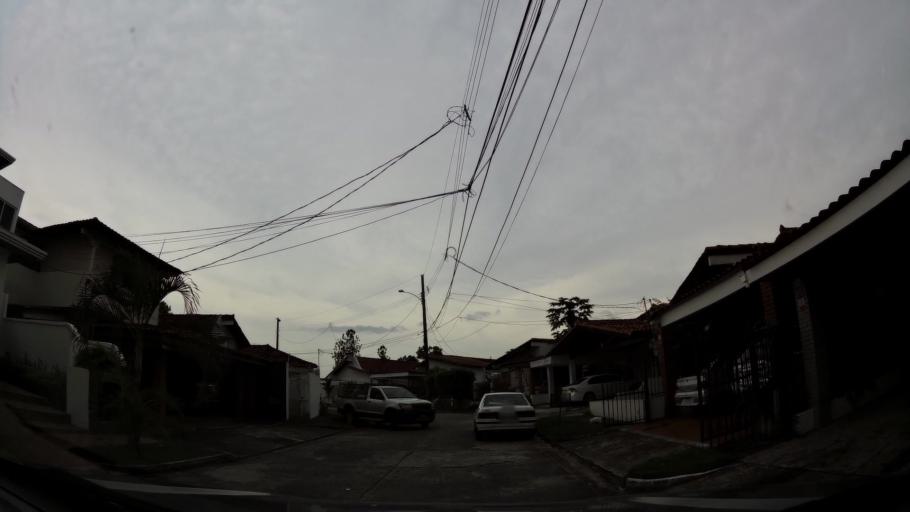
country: PA
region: Panama
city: Panama
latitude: 9.0129
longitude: -79.5382
